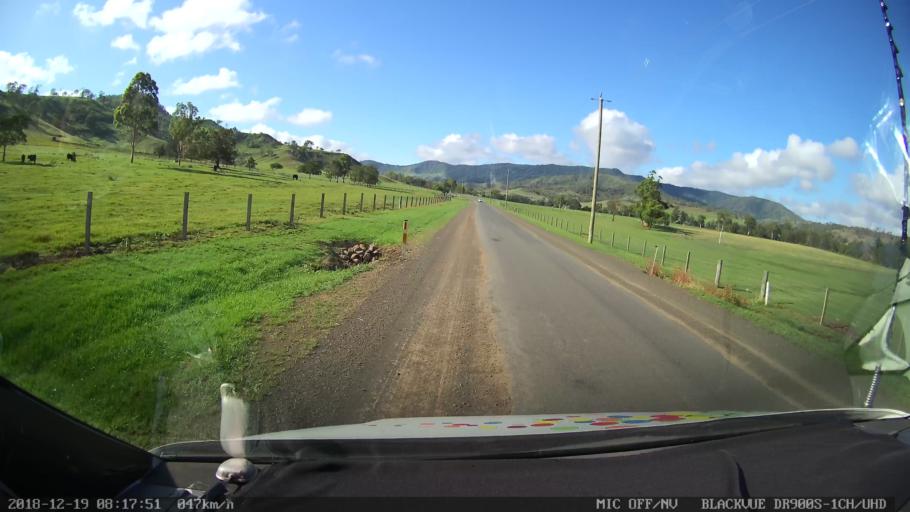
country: AU
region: New South Wales
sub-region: Kyogle
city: Kyogle
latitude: -28.2691
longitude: 152.9100
